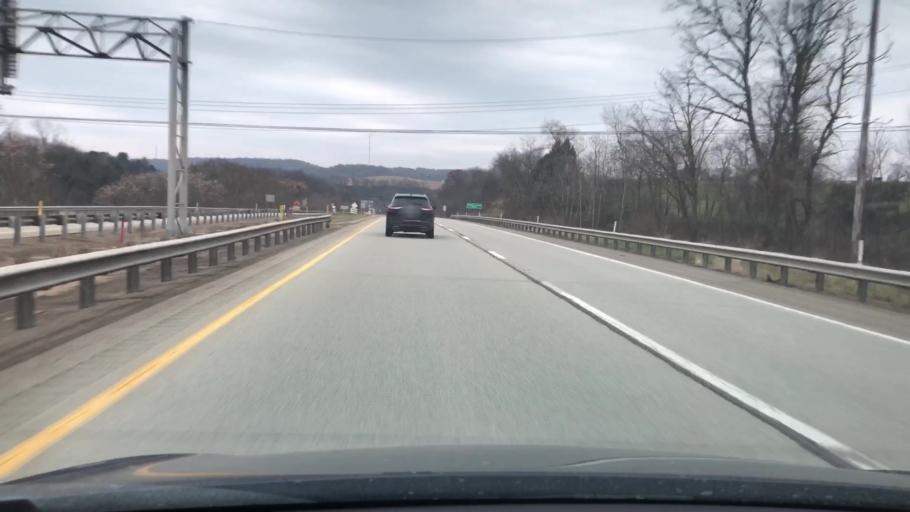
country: US
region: Pennsylvania
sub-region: Armstrong County
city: West Hills
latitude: 40.8084
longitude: -79.5576
